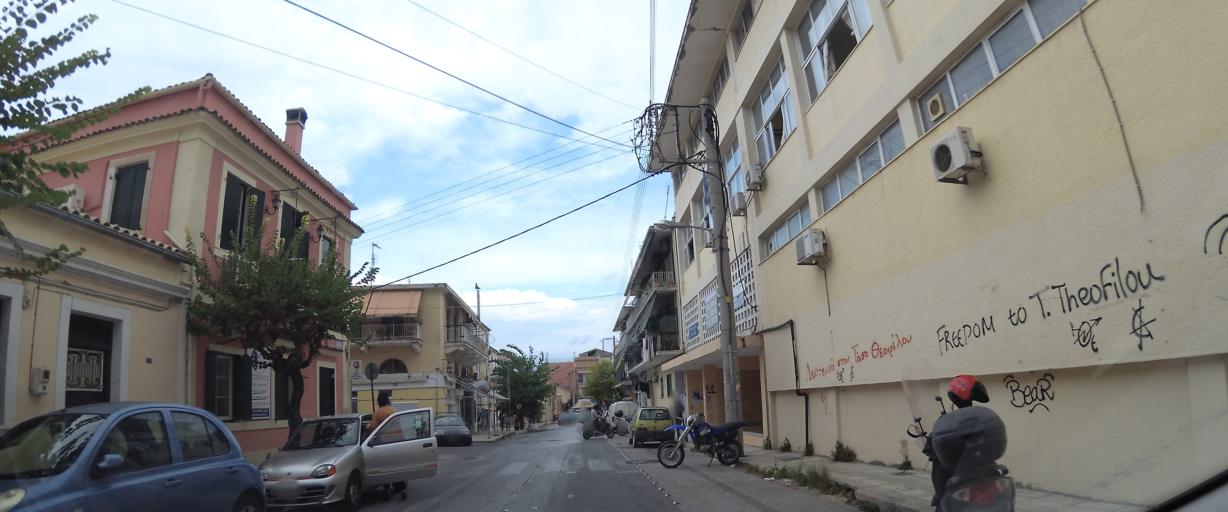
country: GR
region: Ionian Islands
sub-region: Nomos Kerkyras
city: Kerkyra
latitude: 39.6240
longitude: 19.9094
